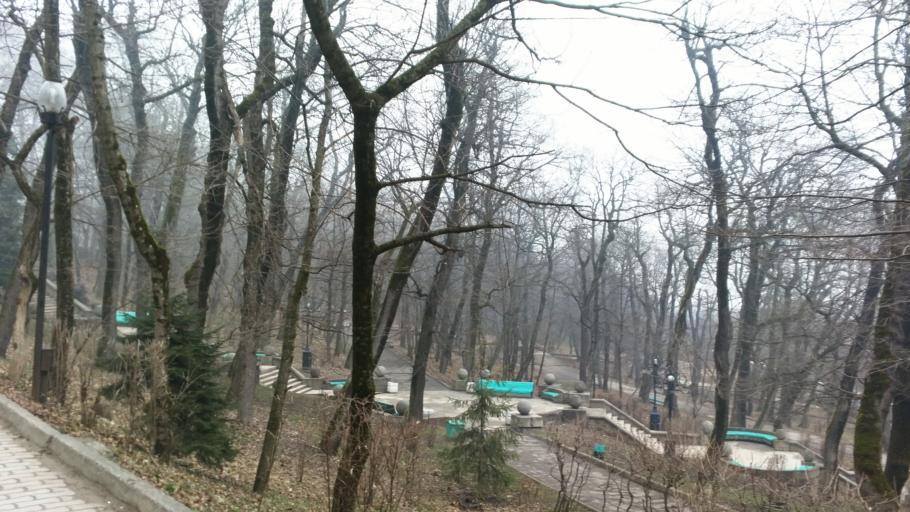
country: RU
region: Stavropol'skiy
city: Zheleznovodsk
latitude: 44.1341
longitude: 43.0303
